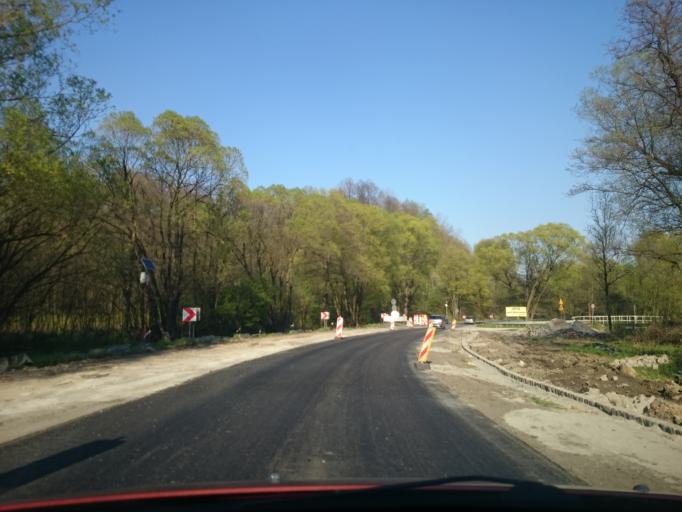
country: PL
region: Lower Silesian Voivodeship
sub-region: Powiat klodzki
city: Duszniki-Zdroj
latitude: 50.4100
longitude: 16.4189
